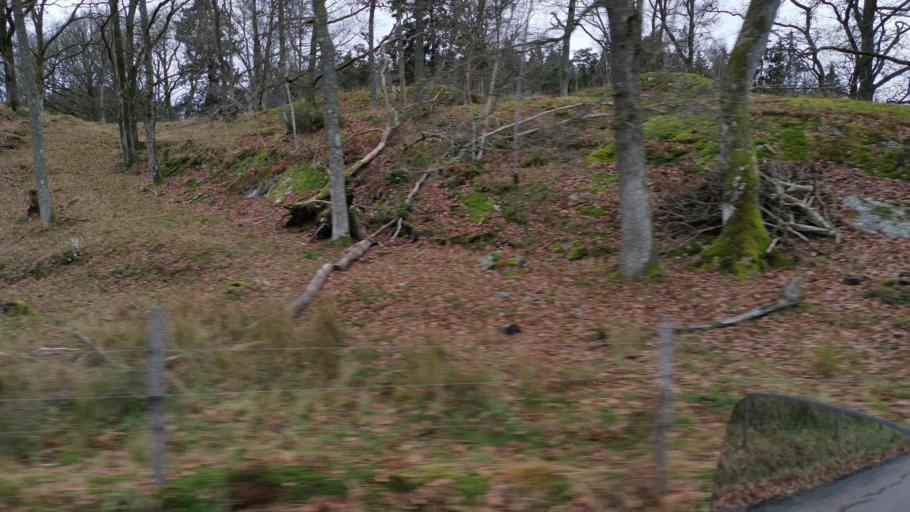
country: SE
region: Vaestra Goetaland
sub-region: Orust
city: Henan
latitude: 58.2074
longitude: 11.7353
